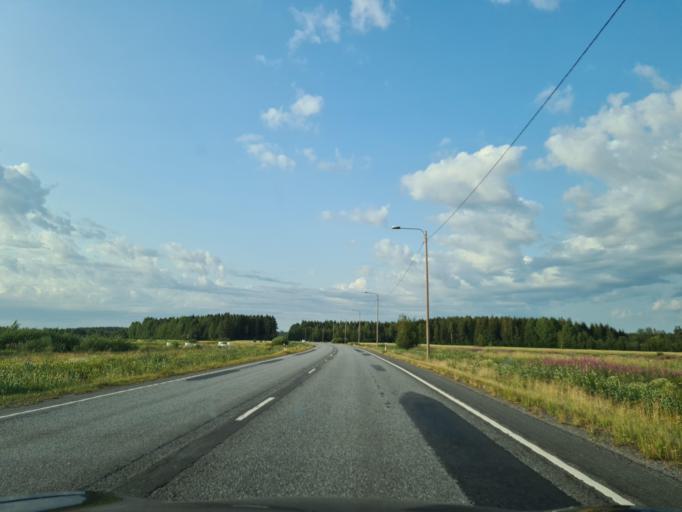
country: FI
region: Southern Ostrobothnia
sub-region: Seinaejoki
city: Kauhava
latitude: 63.0608
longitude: 23.0400
